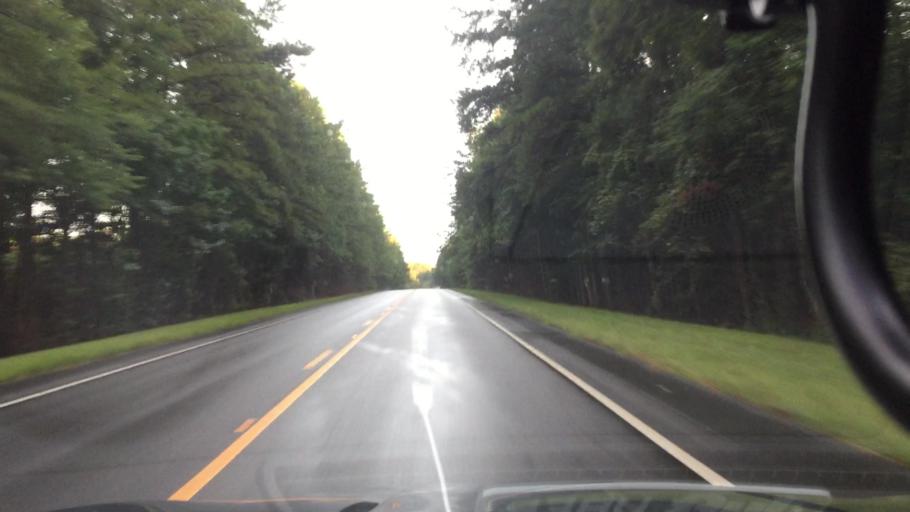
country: US
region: Alabama
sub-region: Coffee County
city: New Brockton
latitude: 31.5604
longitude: -85.9237
